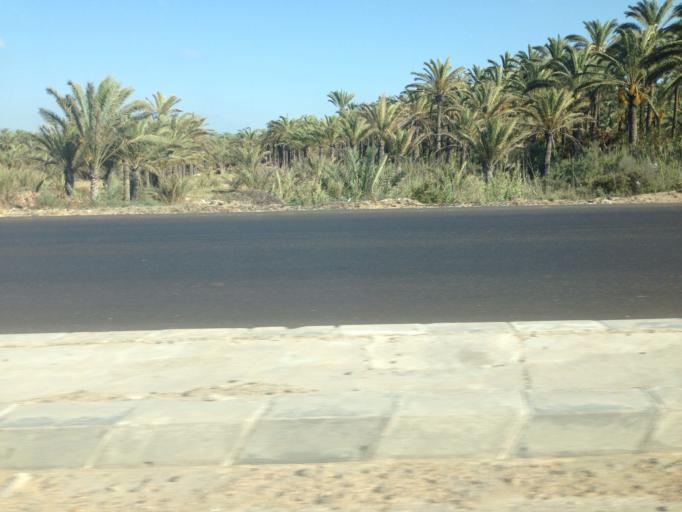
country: EG
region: Al Buhayrah
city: Idku
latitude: 31.2957
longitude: 30.2595
